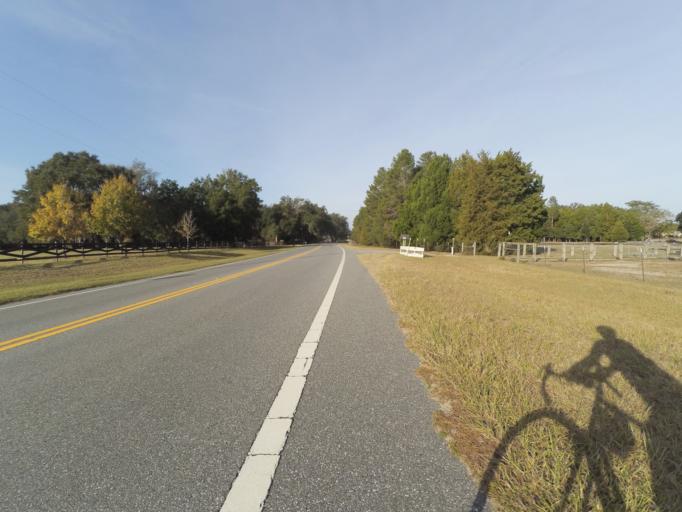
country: US
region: Florida
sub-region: Lake County
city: Umatilla
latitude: 28.9639
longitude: -81.6339
